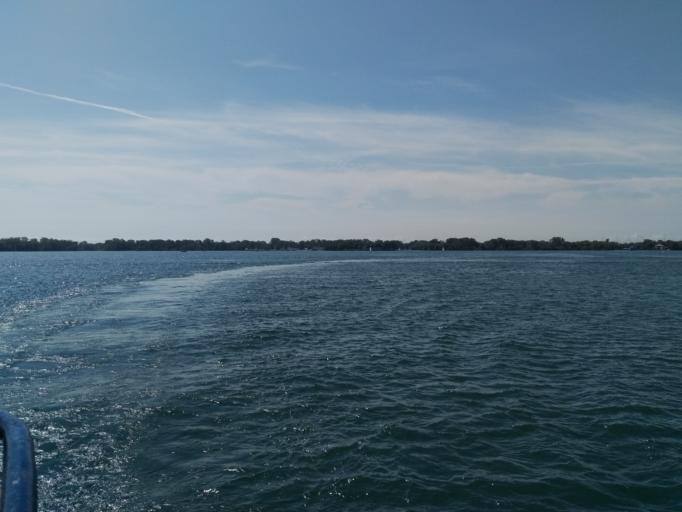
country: CA
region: Ontario
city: Toronto
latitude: 43.6357
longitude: -79.3720
